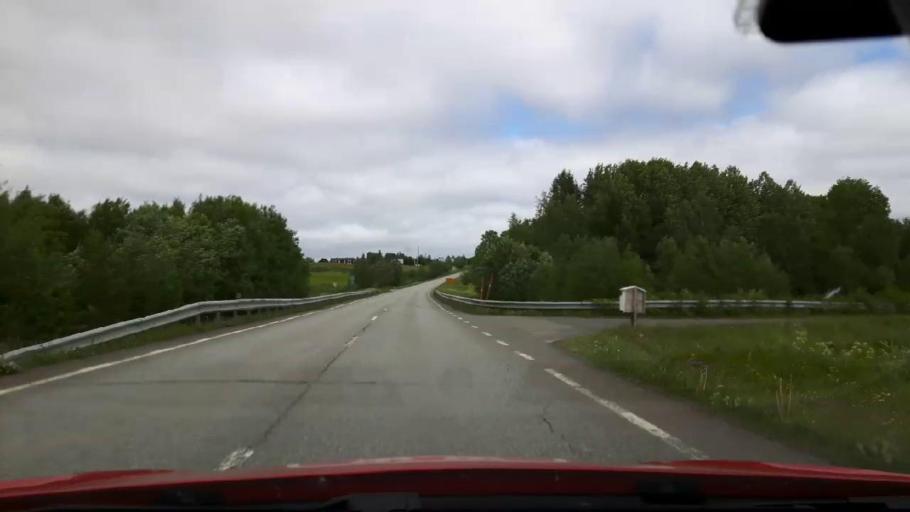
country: SE
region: Jaemtland
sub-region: Krokoms Kommun
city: Krokom
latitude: 63.5140
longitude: 14.5240
